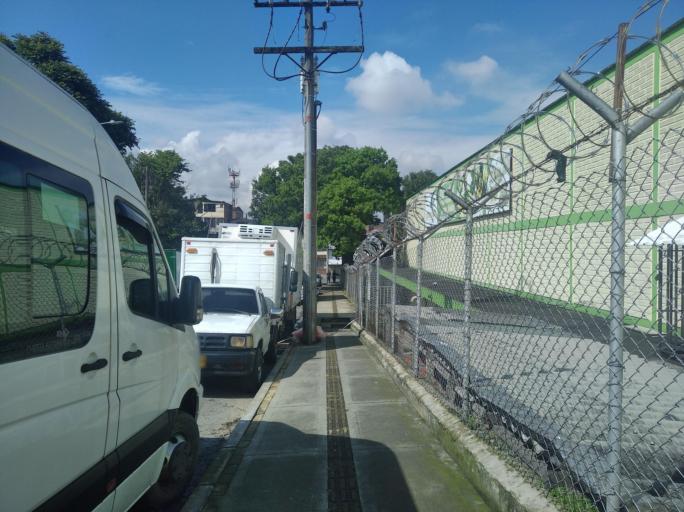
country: CO
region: Antioquia
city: Medellin
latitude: 6.2744
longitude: -75.5585
